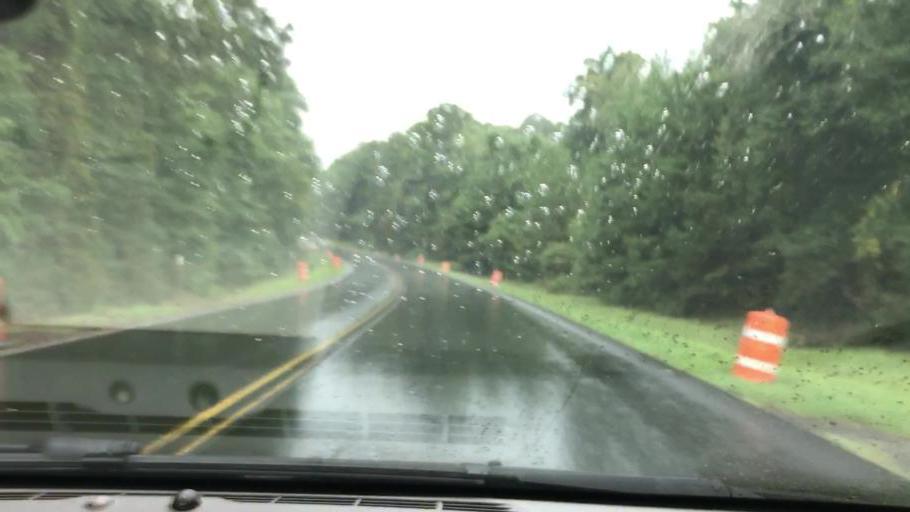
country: US
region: Georgia
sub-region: Clay County
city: Fort Gaines
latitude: 31.5926
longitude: -85.0348
